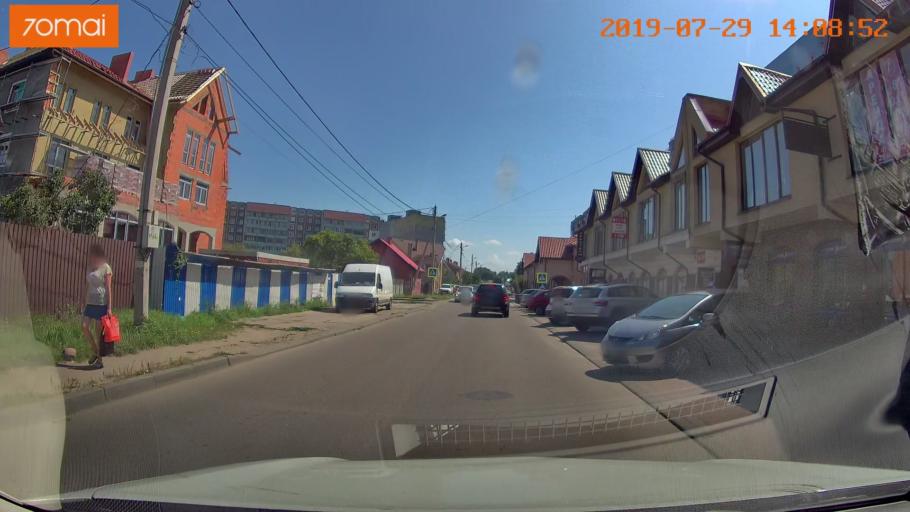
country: RU
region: Kaliningrad
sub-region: Gorod Kaliningrad
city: Baltiysk
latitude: 54.6566
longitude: 19.9079
